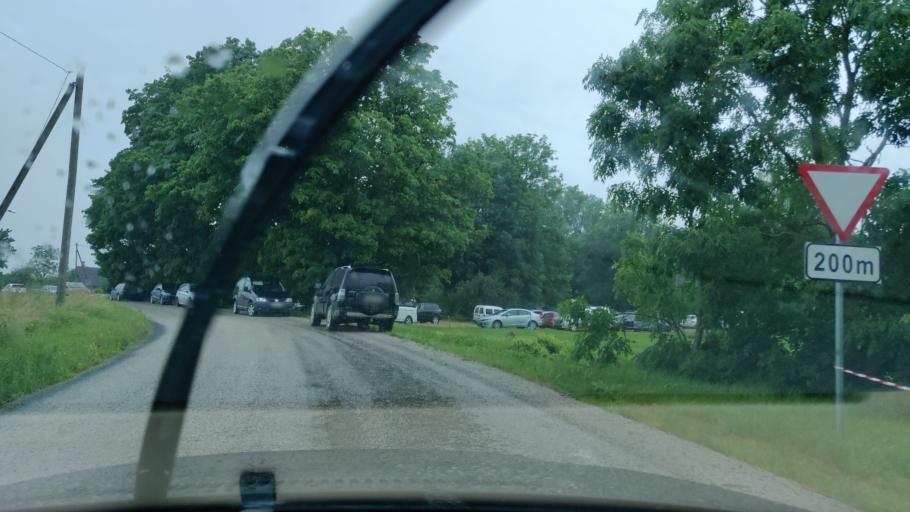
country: EE
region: Jaervamaa
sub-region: Jaerva-Jaani vald
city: Jarva-Jaani
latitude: 59.0951
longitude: 25.6991
